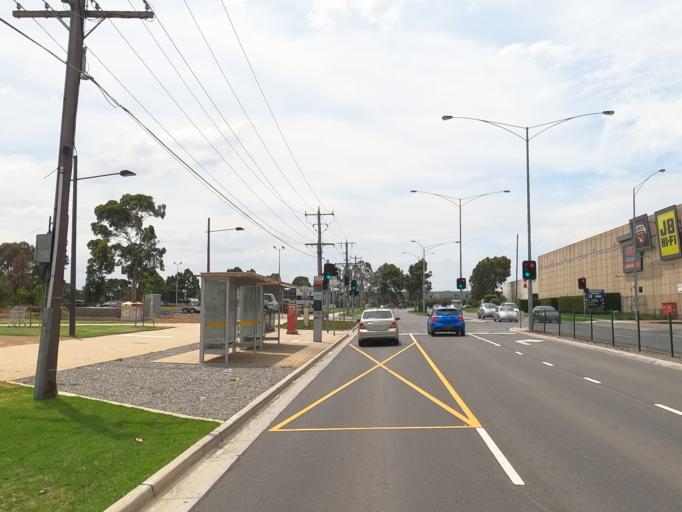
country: AU
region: Victoria
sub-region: Hume
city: Broadmeadows
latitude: -37.6792
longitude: 144.9180
